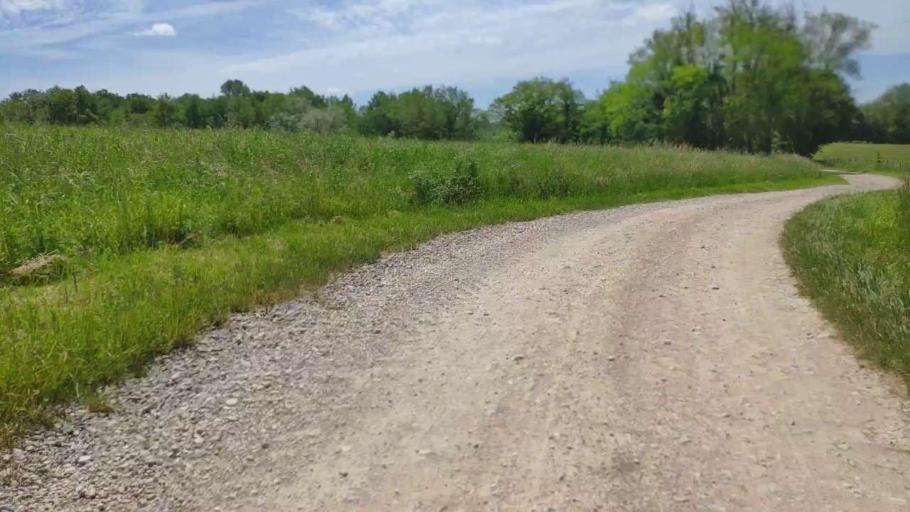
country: FR
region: Franche-Comte
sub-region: Departement du Jura
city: Bletterans
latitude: 46.7871
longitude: 5.3681
